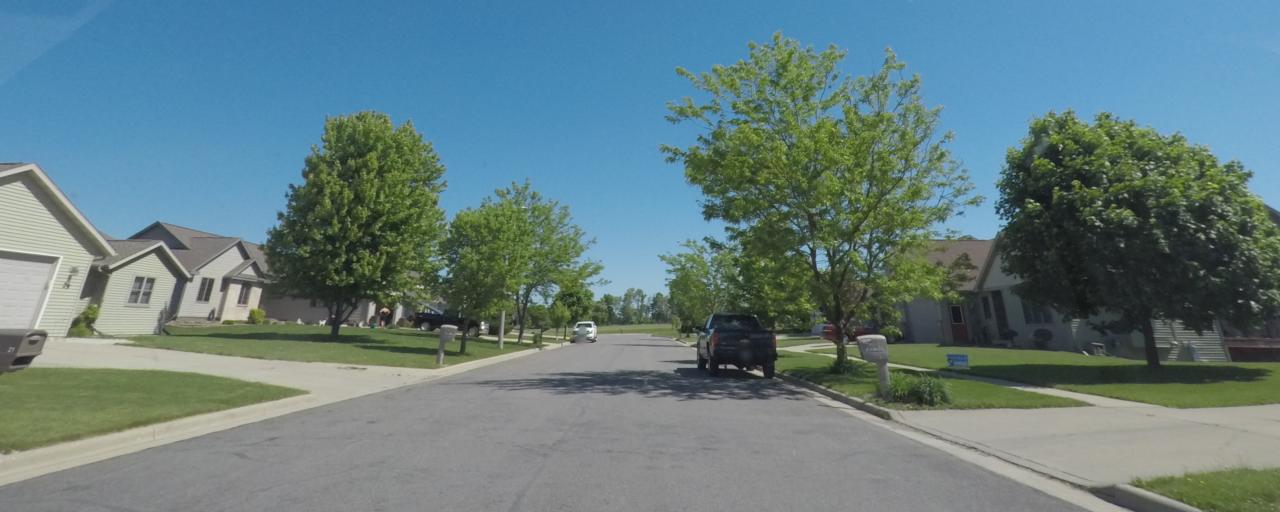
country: US
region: Wisconsin
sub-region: Rock County
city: Evansville
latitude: 42.7810
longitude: -89.3215
